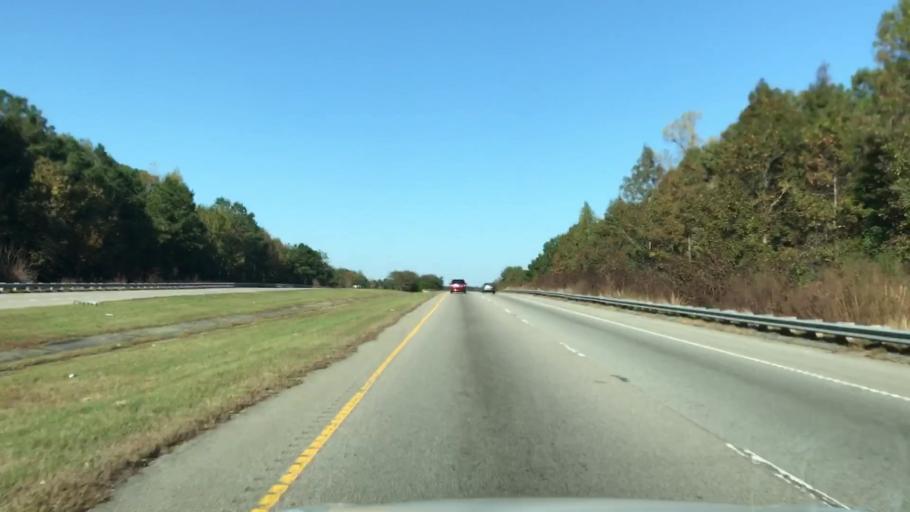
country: US
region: South Carolina
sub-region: Charleston County
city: Shell Point
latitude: 32.8221
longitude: -80.0722
